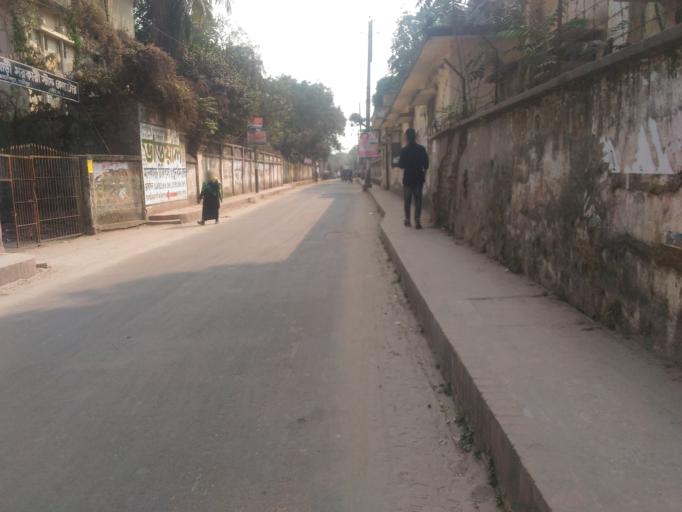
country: BD
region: Dhaka
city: Tungi
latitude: 24.0011
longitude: 90.4260
